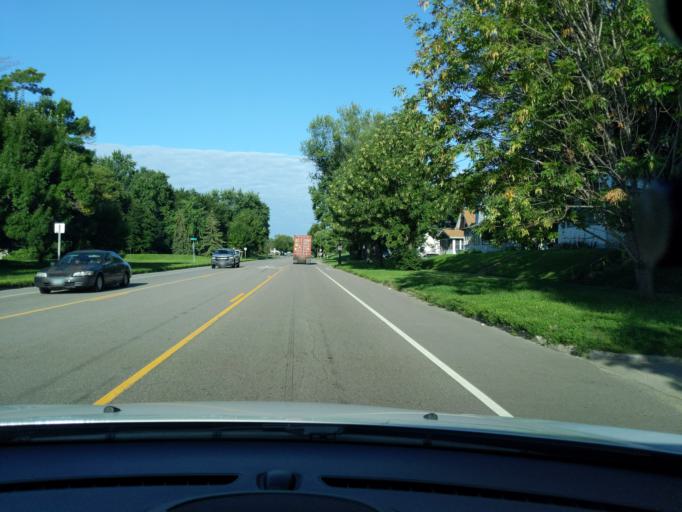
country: US
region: Minnesota
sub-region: Ramsey County
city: Falcon Heights
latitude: 44.9648
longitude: -93.1329
